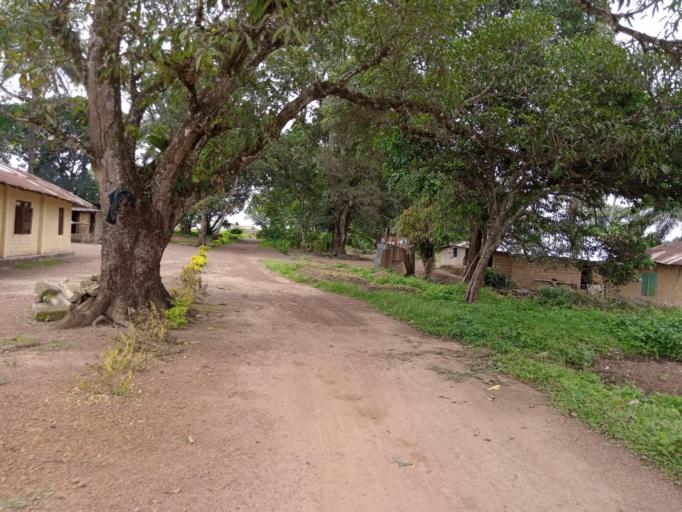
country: SL
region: Southern Province
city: Moyamba
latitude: 8.1621
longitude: -12.4258
